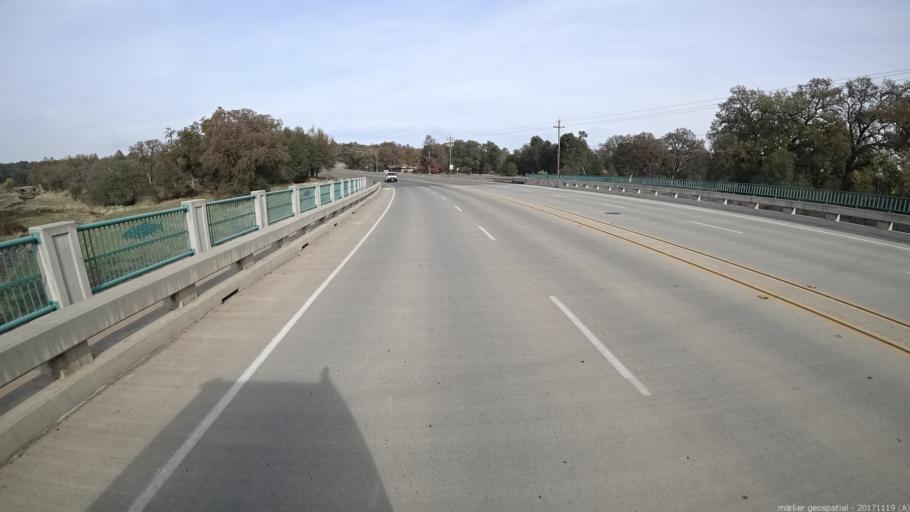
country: US
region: California
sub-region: Shasta County
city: Anderson
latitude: 40.4742
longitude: -122.2930
